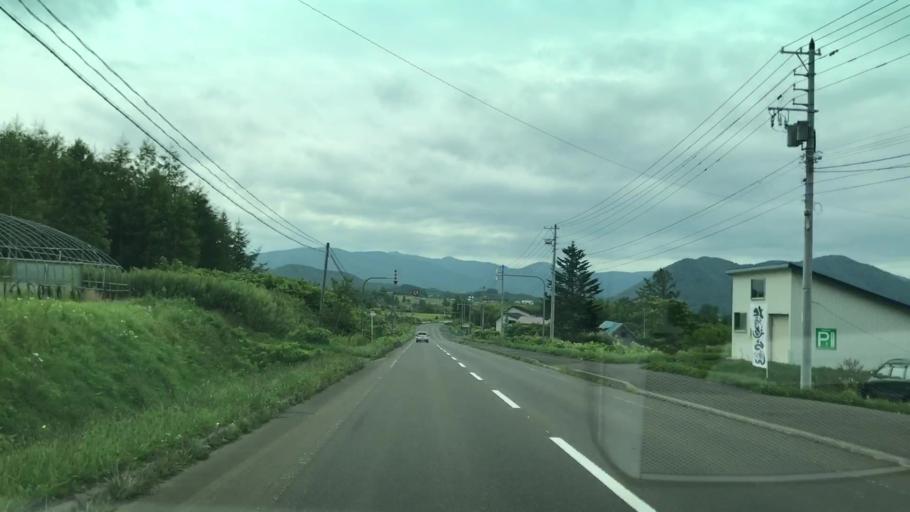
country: JP
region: Hokkaido
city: Yoichi
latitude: 43.1029
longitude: 140.8236
